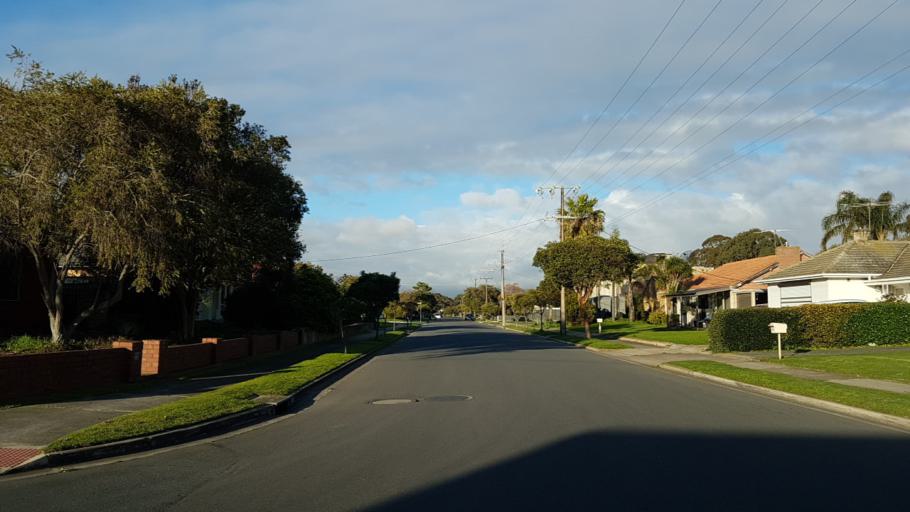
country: AU
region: South Australia
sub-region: Charles Sturt
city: Henley Beach
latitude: -34.9316
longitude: 138.5120
